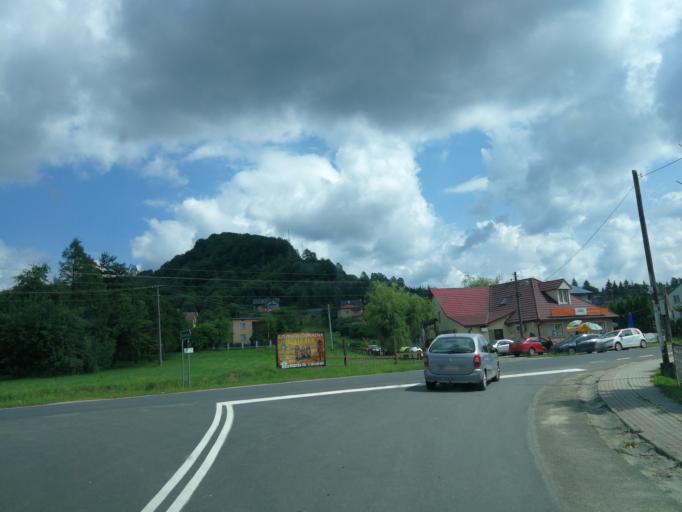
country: PL
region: Subcarpathian Voivodeship
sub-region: Powiat leski
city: Polanczyk
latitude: 49.4140
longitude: 22.4490
